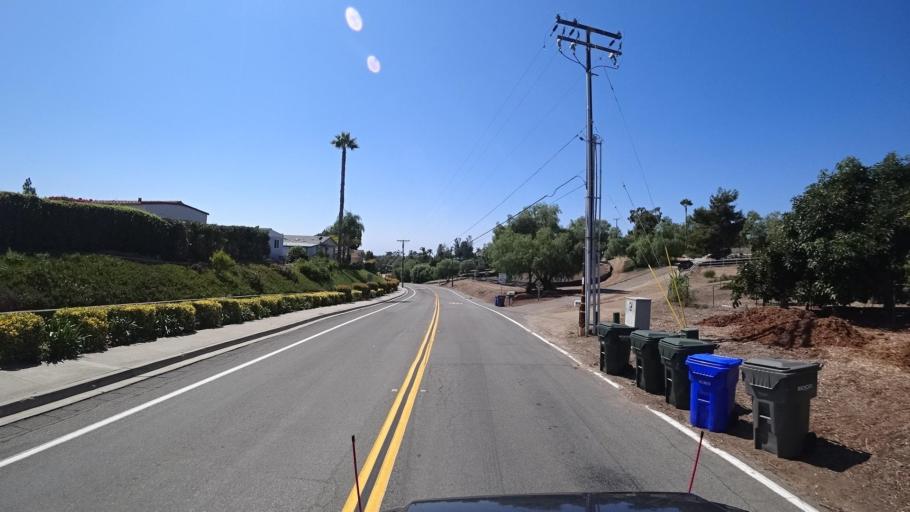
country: US
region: California
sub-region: San Diego County
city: Lake San Marcos
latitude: 33.1417
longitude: -117.2118
